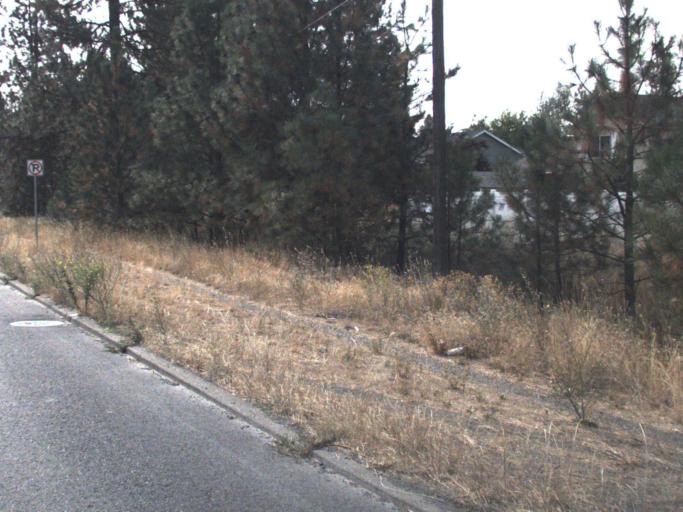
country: US
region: Washington
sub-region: Spokane County
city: Town and Country
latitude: 47.7277
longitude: -117.4979
